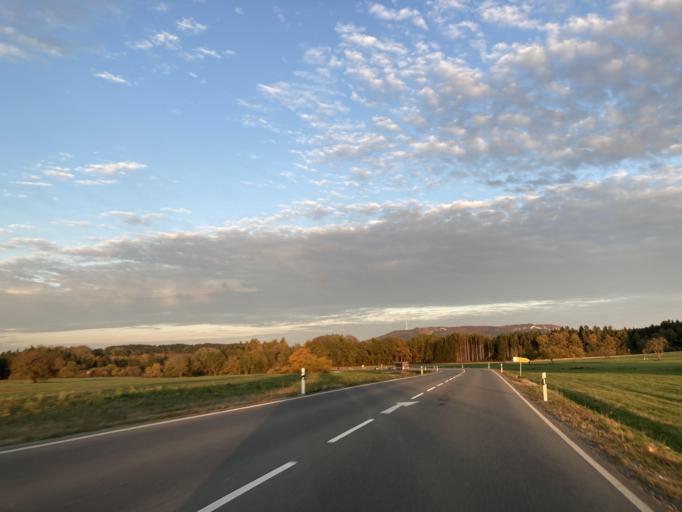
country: DE
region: Baden-Wuerttemberg
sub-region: Tuebingen Region
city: Zimmern unter der Burg
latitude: 48.2021
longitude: 8.7150
